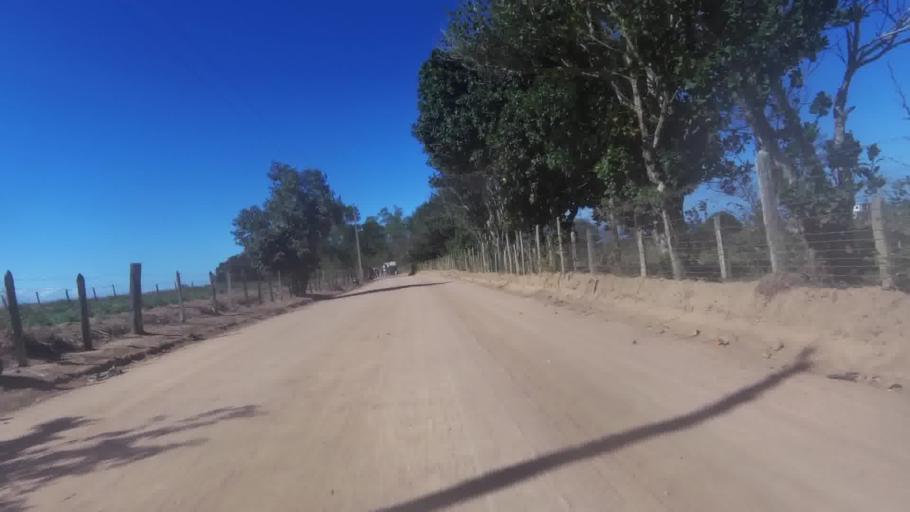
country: BR
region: Espirito Santo
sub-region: Marataizes
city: Marataizes
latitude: -21.1344
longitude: -40.9898
